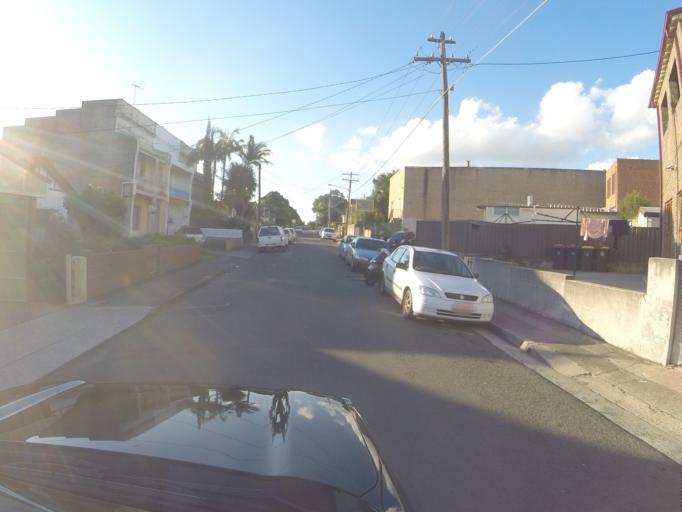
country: AU
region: New South Wales
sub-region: Canterbury
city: Canterbury
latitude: -33.9104
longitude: 151.1212
